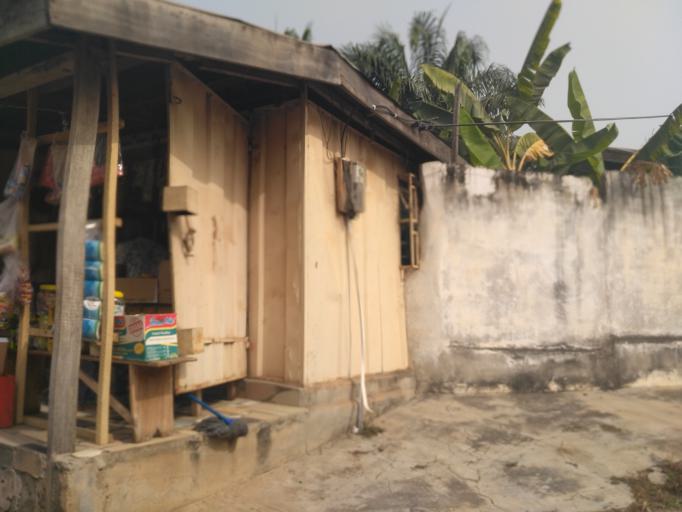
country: GH
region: Ashanti
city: Kumasi
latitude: 6.6753
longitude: -1.6042
